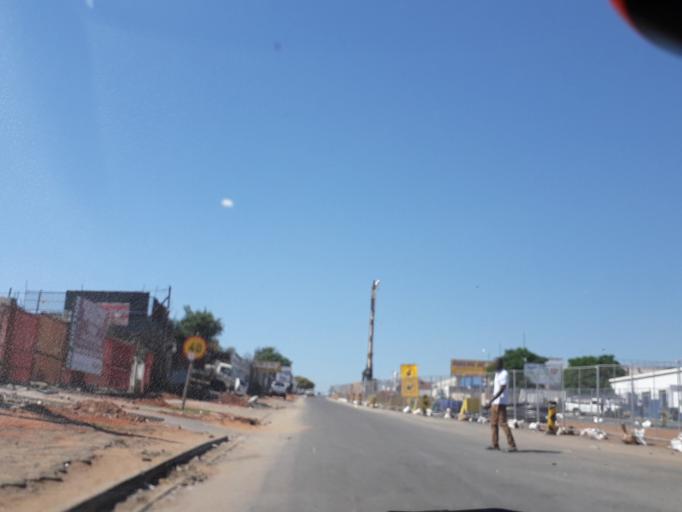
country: ZA
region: Gauteng
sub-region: City of Johannesburg Metropolitan Municipality
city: Modderfontein
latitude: -26.1111
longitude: 28.0849
